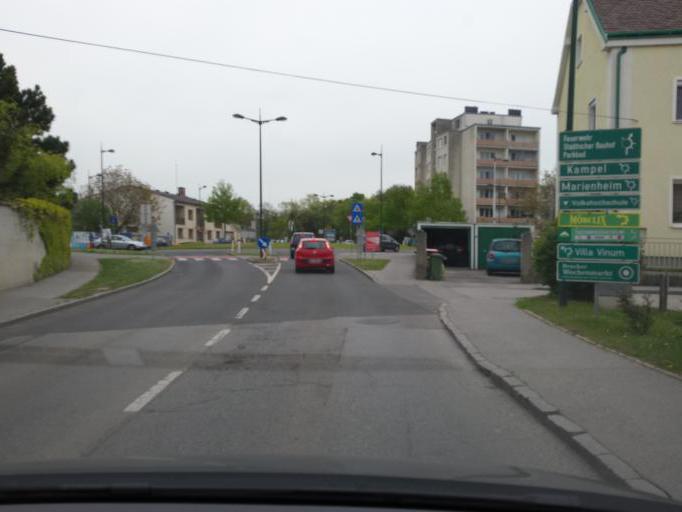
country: AT
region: Burgenland
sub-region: Politischer Bezirk Neusiedl am See
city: Bruckneudorf
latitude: 48.0284
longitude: 16.7794
